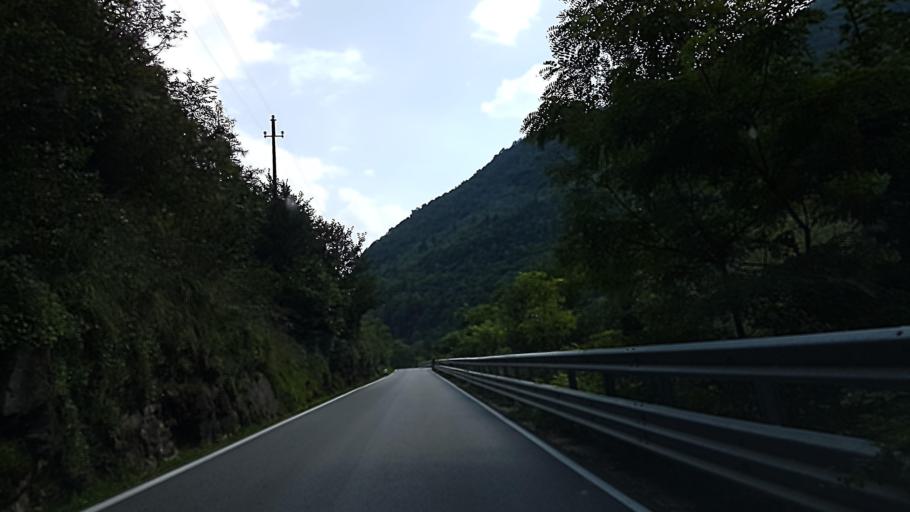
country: IT
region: Lombardy
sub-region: Provincia di Sondrio
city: San Giacomo Filippo
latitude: 46.3294
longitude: 9.3747
